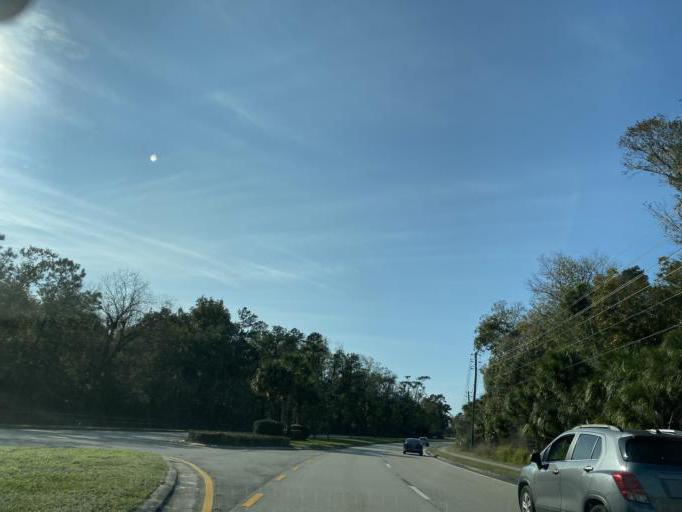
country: US
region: Florida
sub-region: Seminole County
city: Longwood
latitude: 28.7267
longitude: -81.3245
